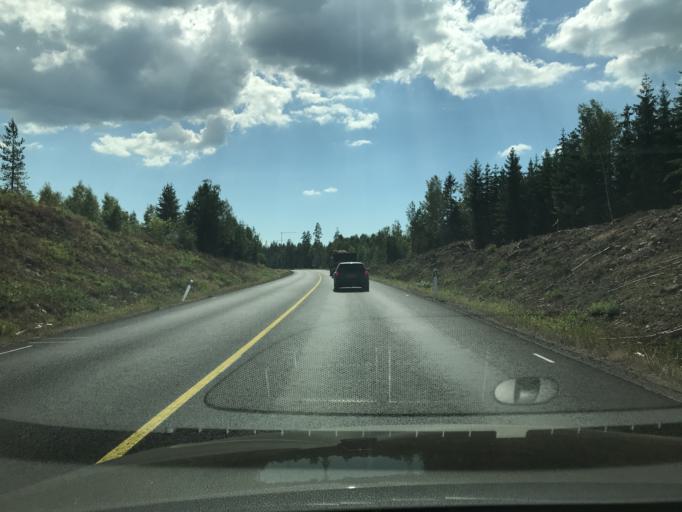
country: SE
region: Kronoberg
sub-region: Almhults Kommun
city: AElmhult
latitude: 56.5902
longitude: 14.1966
